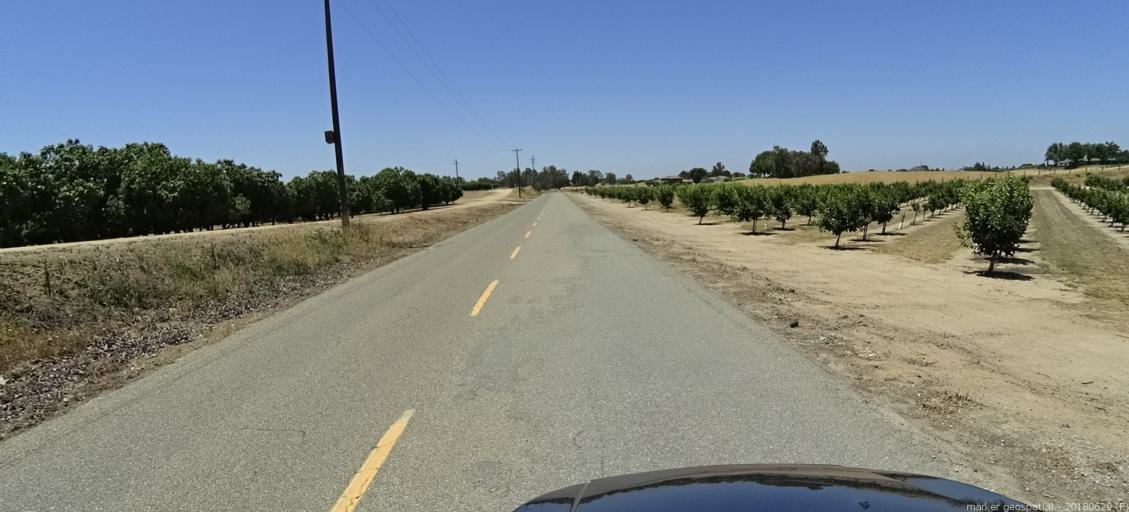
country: US
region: California
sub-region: Madera County
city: Parksdale
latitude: 37.0093
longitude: -119.9724
